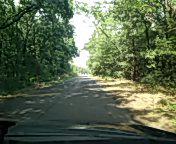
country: HU
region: Hajdu-Bihar
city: Hajdusamson
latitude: 47.5255
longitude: 21.7343
